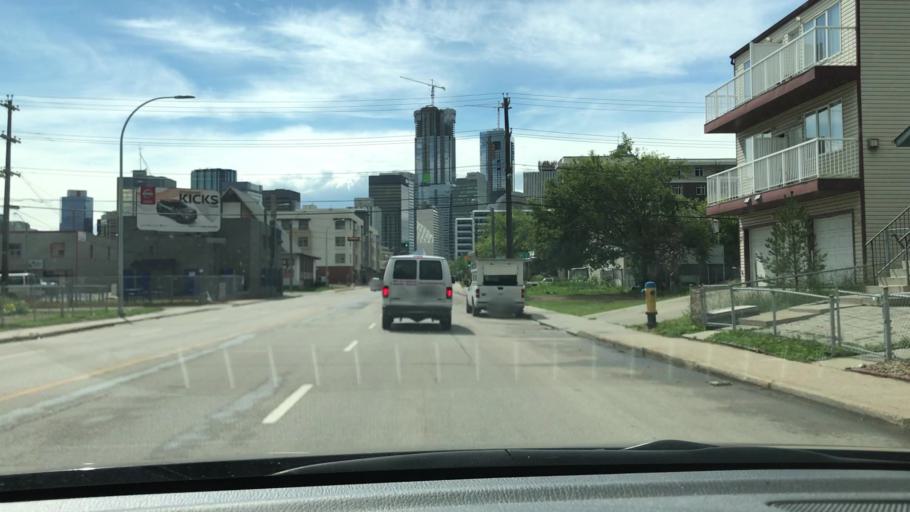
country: CA
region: Alberta
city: Edmonton
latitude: 53.5482
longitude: -113.4787
